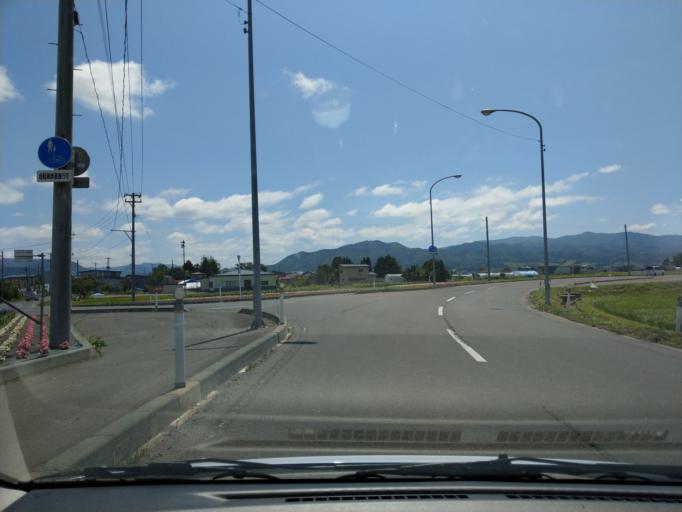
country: JP
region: Aomori
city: Kuroishi
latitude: 40.5770
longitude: 140.5516
